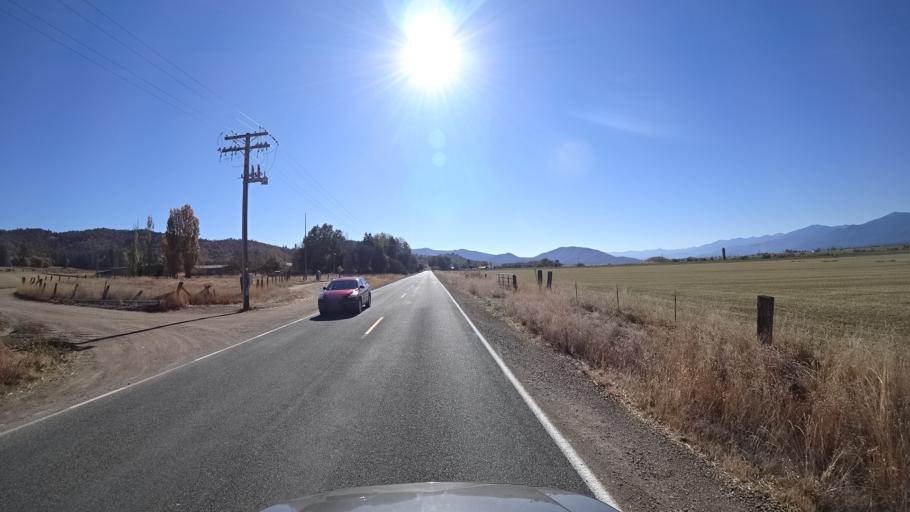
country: US
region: California
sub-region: Siskiyou County
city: Yreka
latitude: 41.5961
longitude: -122.8425
